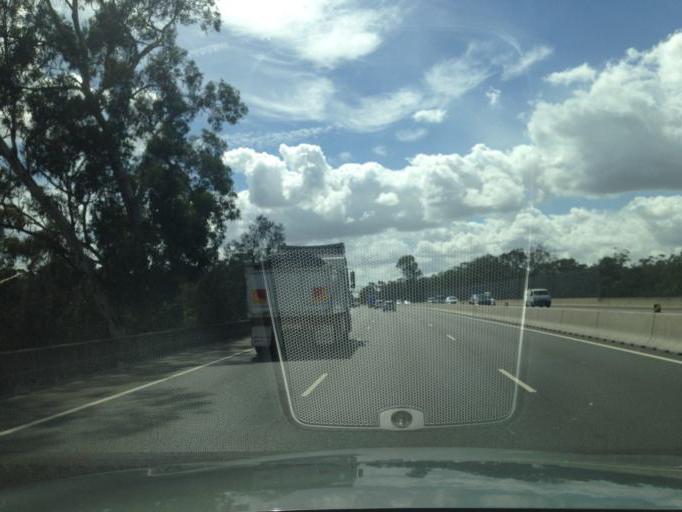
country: AU
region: New South Wales
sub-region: Bankstown
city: Milperra
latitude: -33.9472
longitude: 150.9690
